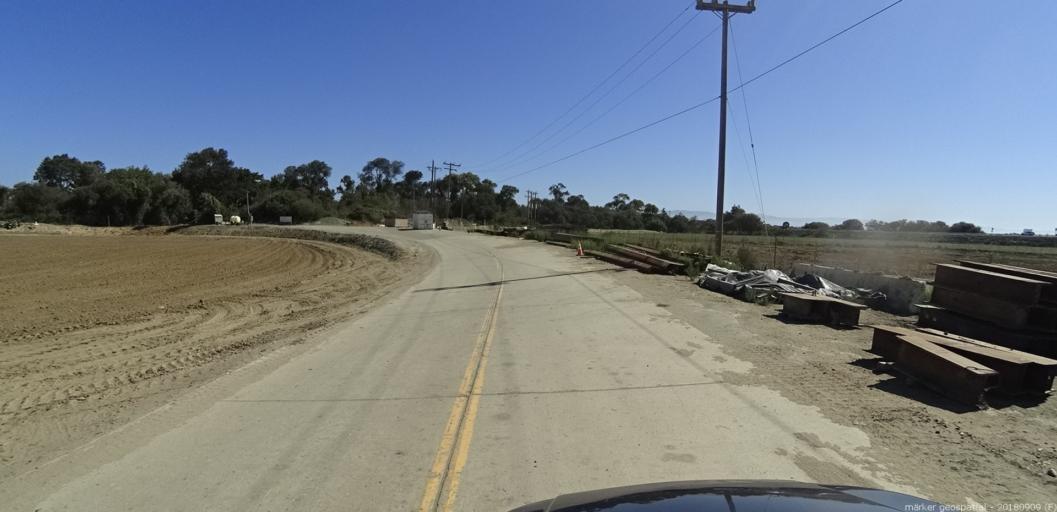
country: US
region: California
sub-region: Monterey County
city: Salinas
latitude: 36.6281
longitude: -121.6803
